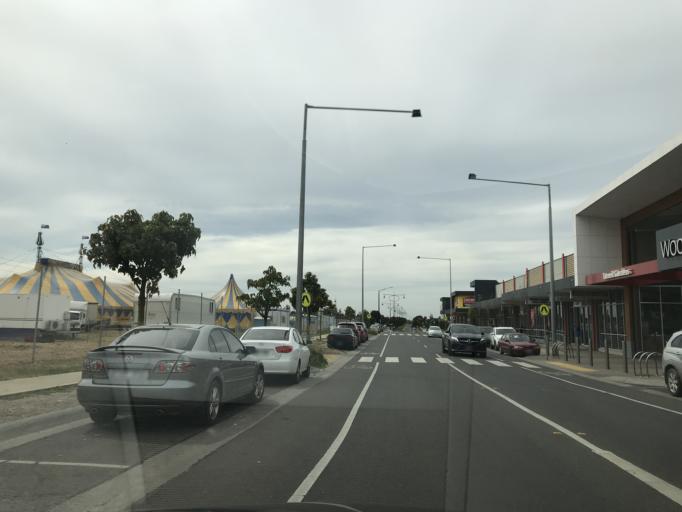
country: AU
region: Victoria
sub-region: Wyndham
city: Tarneit
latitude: -37.8394
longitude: 144.6735
